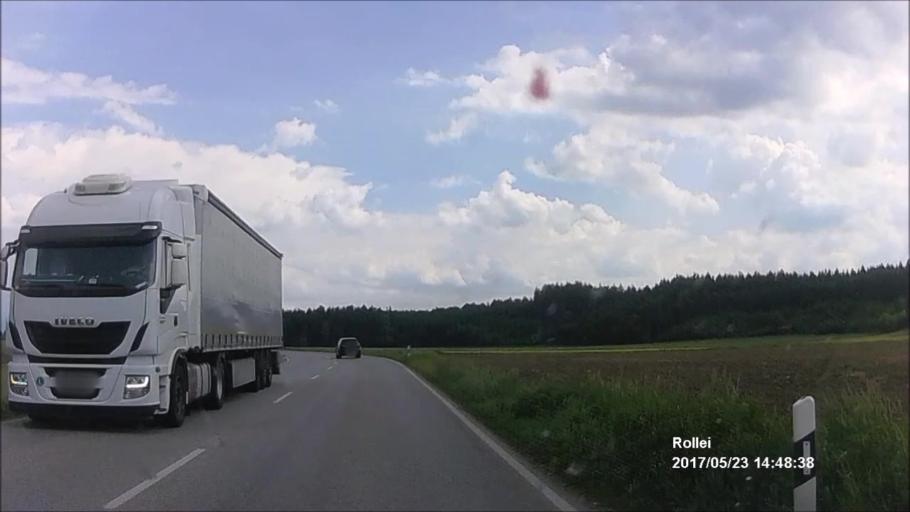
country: DE
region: Bavaria
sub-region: Upper Bavaria
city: Traunreut
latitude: 47.9557
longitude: 12.5683
